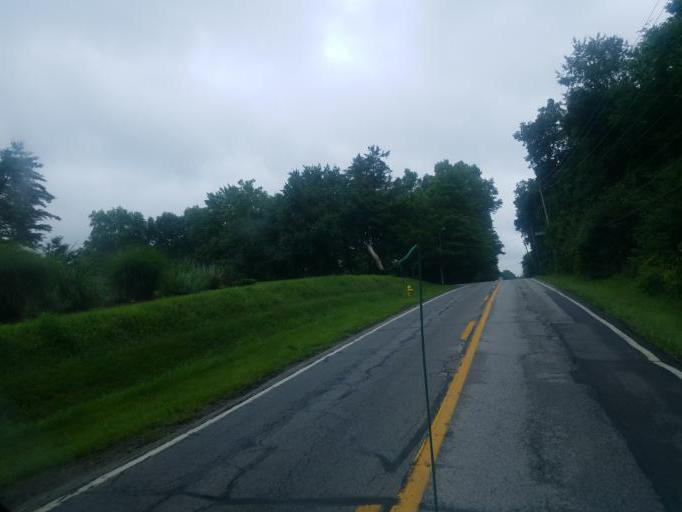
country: US
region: Ohio
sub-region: Franklin County
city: Gahanna
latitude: 40.0093
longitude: -82.8341
